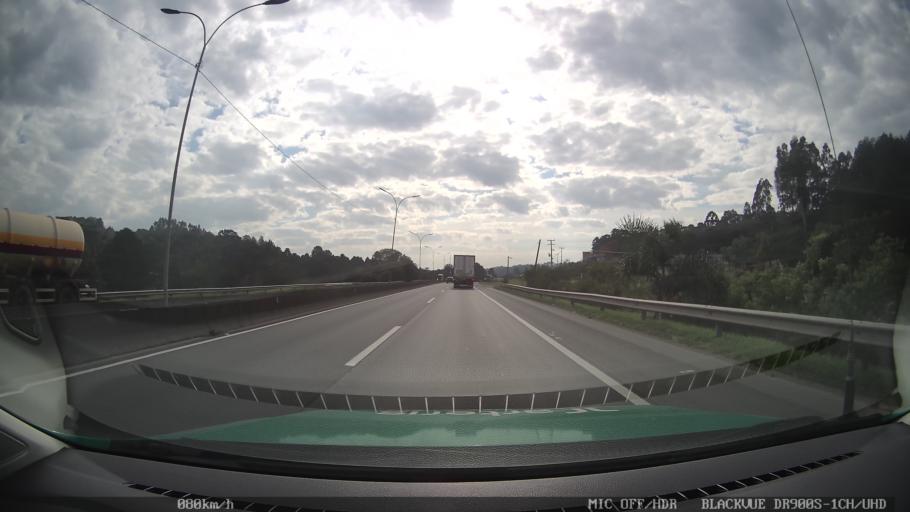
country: BR
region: Parana
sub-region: Campina Grande Do Sul
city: Campina Grande do Sul
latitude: -25.3222
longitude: -49.0256
